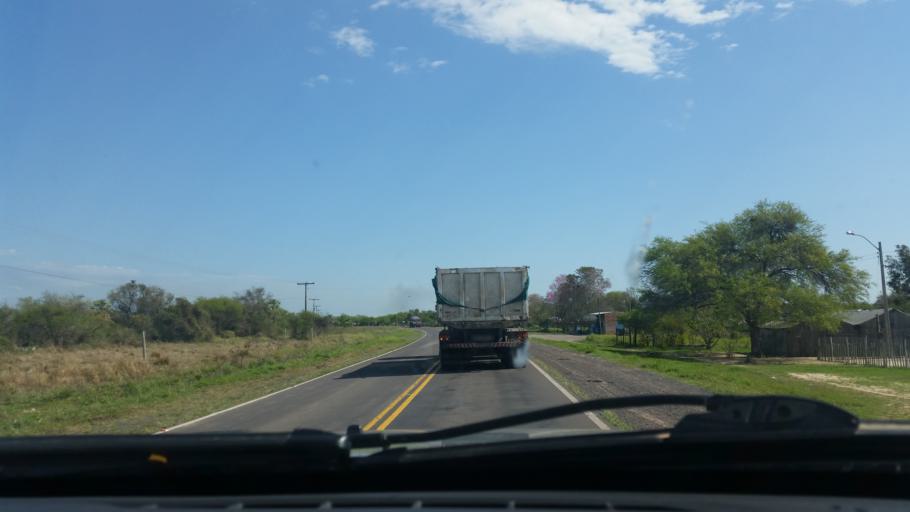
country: PY
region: Presidente Hayes
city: Benjamin Aceval
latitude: -24.4315
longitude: -58.0471
